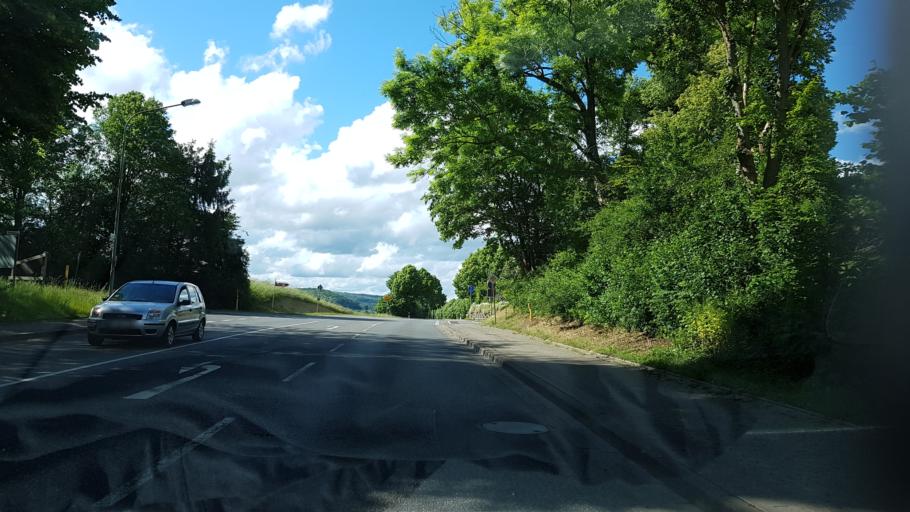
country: DE
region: Lower Saxony
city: Bovenden
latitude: 51.5897
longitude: 9.8705
